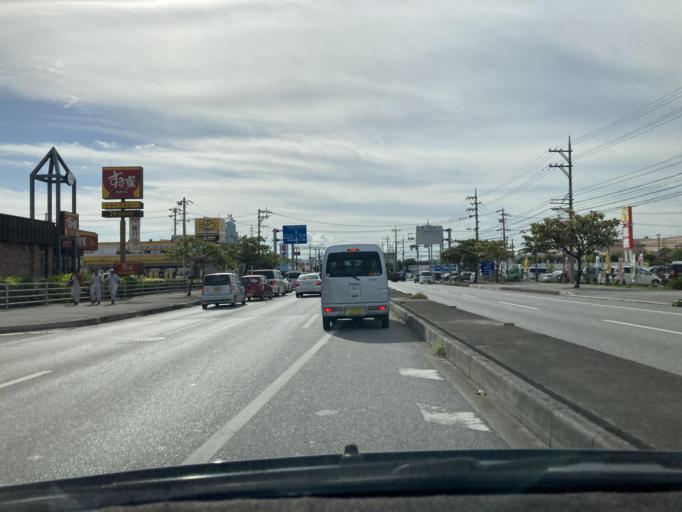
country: JP
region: Okinawa
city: Katsuren-haebaru
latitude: 26.3386
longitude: 127.8480
